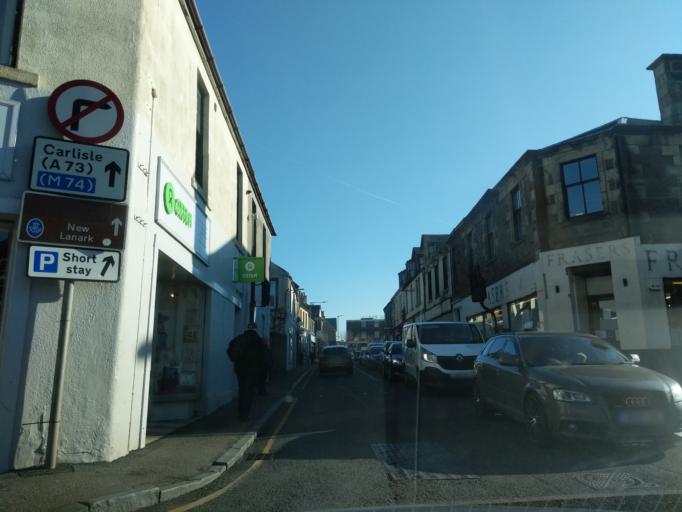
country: GB
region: Scotland
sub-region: South Lanarkshire
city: Lanark
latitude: 55.6737
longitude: -3.7757
